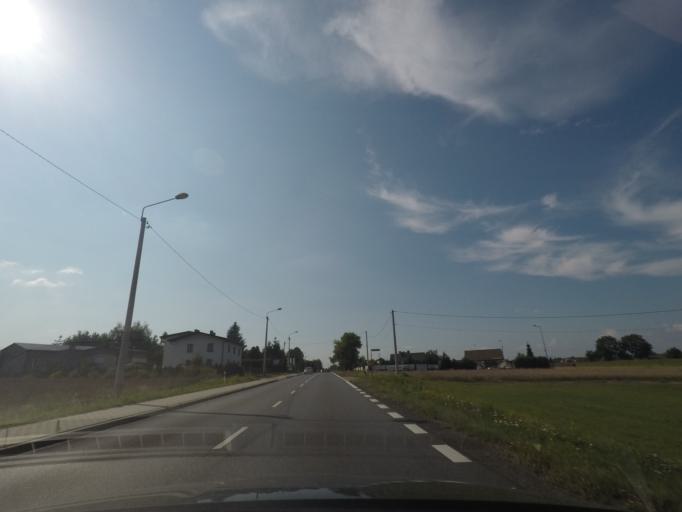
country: PL
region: Silesian Voivodeship
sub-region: Powiat pszczynski
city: Radostowice
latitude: 50.0040
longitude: 18.8757
